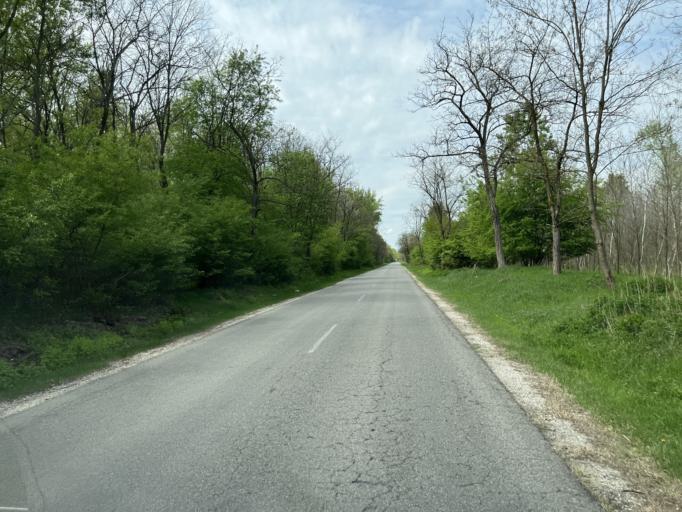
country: HU
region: Pest
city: Csemo
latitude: 47.1531
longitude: 19.6180
